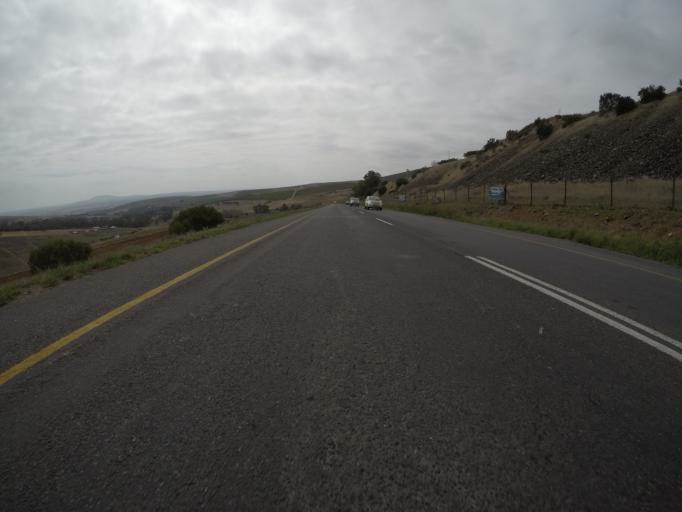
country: ZA
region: Western Cape
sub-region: City of Cape Town
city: Sunset Beach
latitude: -33.8312
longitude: 18.5894
